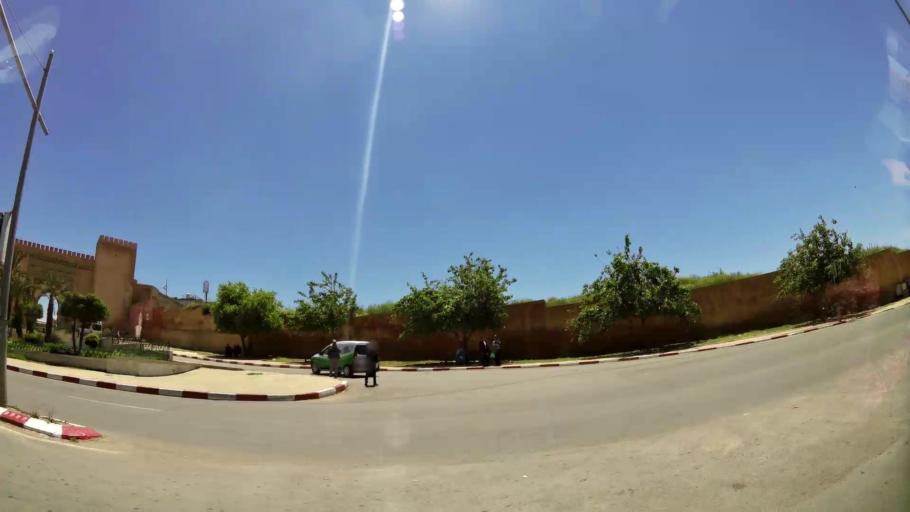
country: MA
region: Meknes-Tafilalet
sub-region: Meknes
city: Meknes
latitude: 33.9017
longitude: -5.5688
